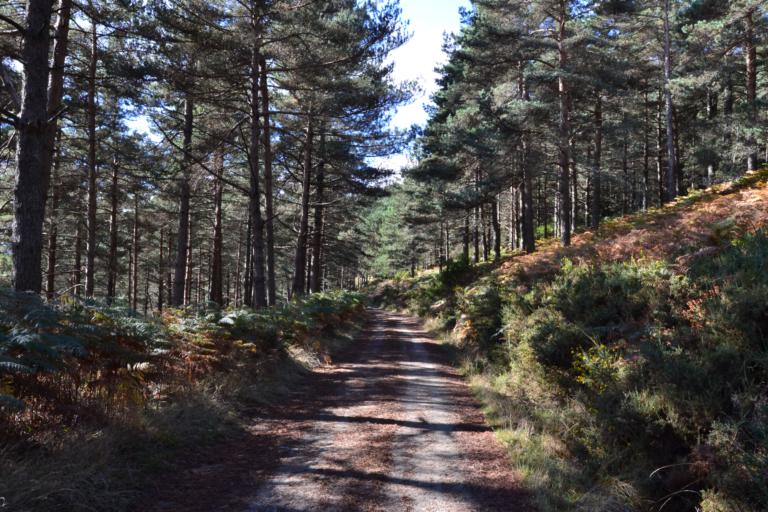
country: PT
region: Vila Real
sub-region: Mondim de Basto
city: Mondim de Basto
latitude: 41.3162
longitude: -7.8896
